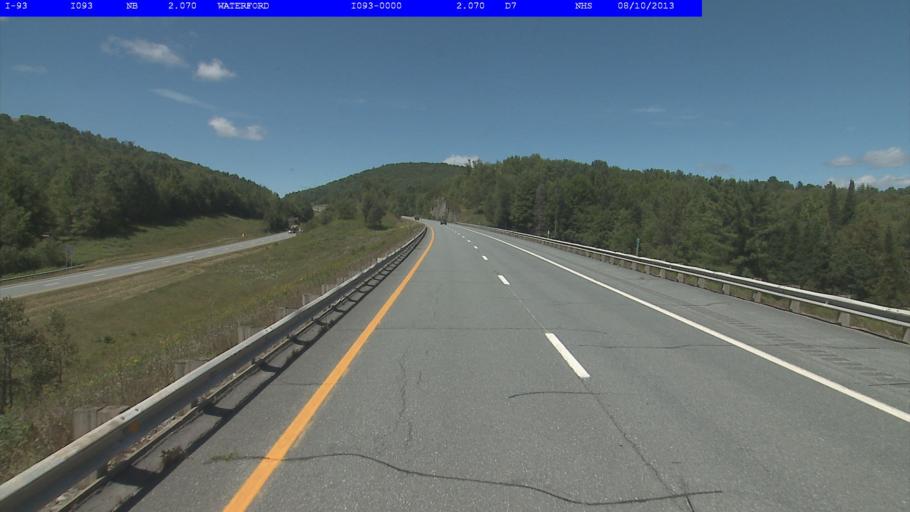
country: US
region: Vermont
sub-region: Caledonia County
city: Saint Johnsbury
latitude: 44.3710
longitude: -71.9055
